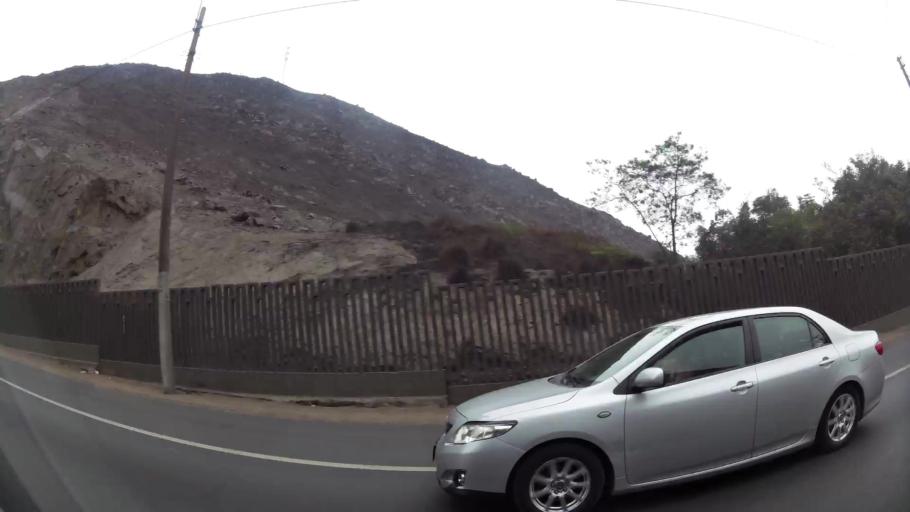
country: PE
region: Lima
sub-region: Lima
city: Vitarte
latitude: -12.0300
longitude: -76.9810
